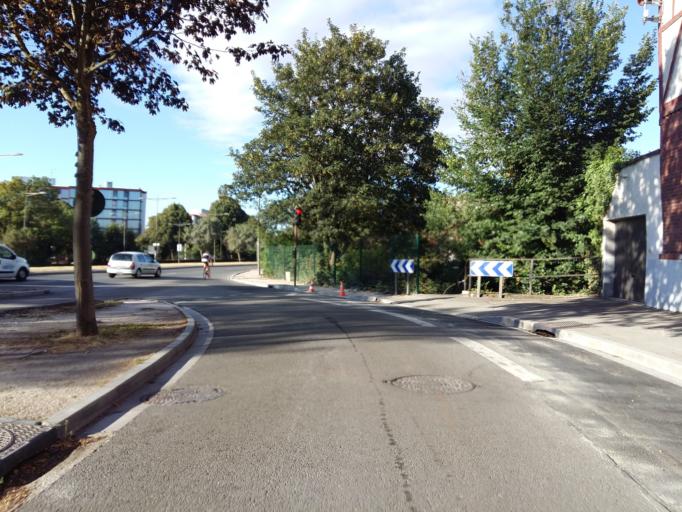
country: FR
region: Picardie
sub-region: Departement de la Somme
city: Rivery
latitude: 49.9006
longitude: 2.3134
